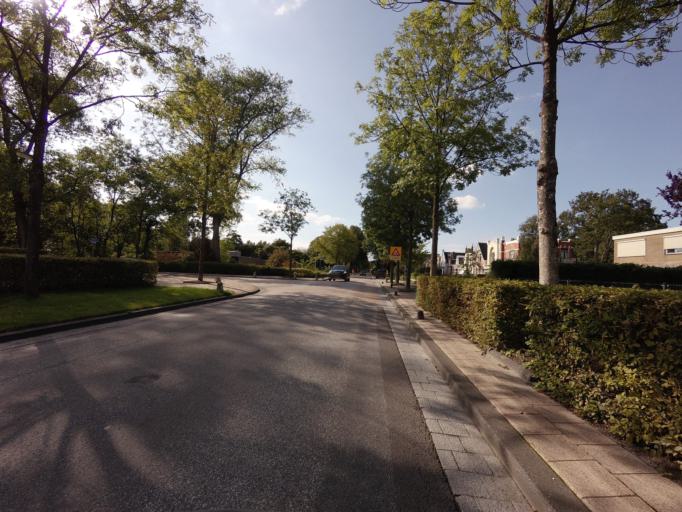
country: NL
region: Friesland
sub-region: Sudwest Fryslan
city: Bolsward
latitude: 53.0607
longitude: 5.5337
